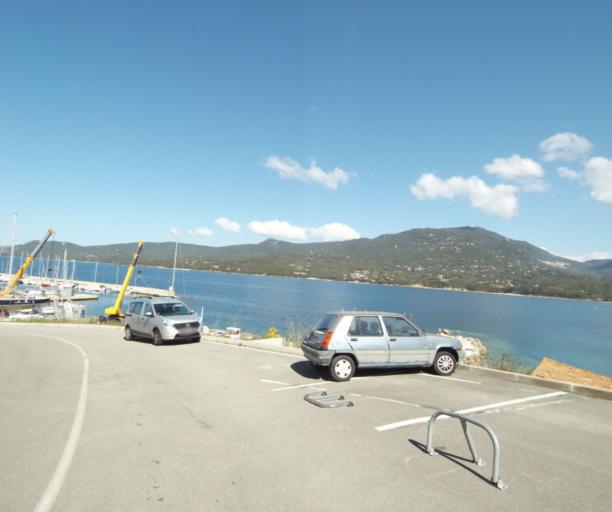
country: FR
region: Corsica
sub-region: Departement de la Corse-du-Sud
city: Propriano
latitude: 41.6767
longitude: 8.9075
